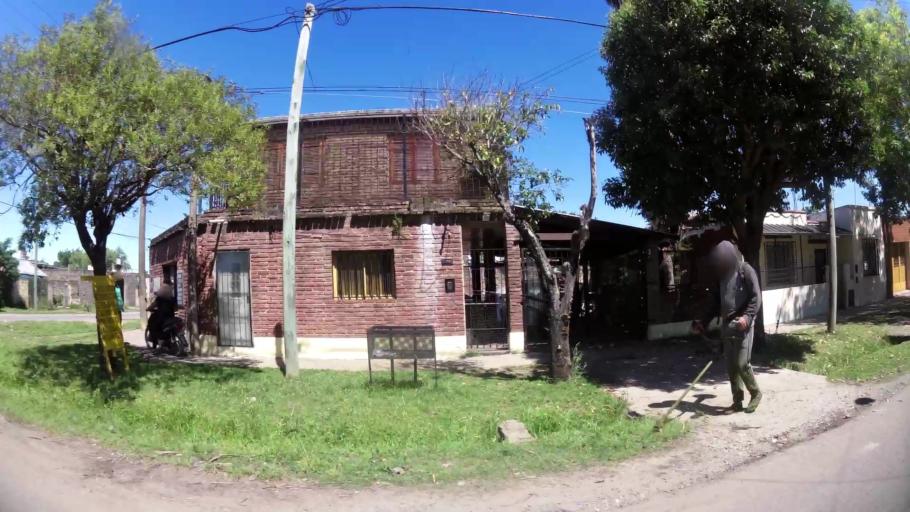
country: AR
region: Santa Fe
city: Perez
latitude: -32.9557
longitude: -60.7155
